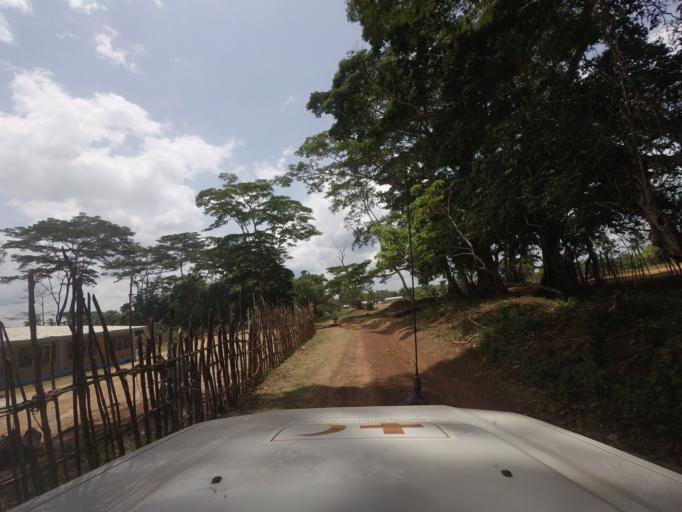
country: LR
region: Bong
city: Gbarnga
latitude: 7.1935
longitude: -9.2054
